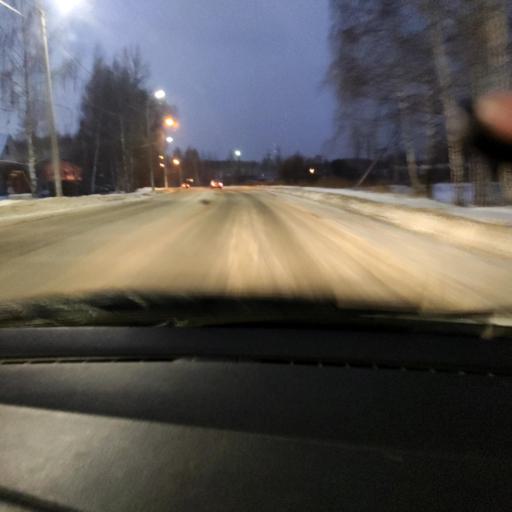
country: RU
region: Tatarstan
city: Aysha
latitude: 55.8711
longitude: 48.5756
